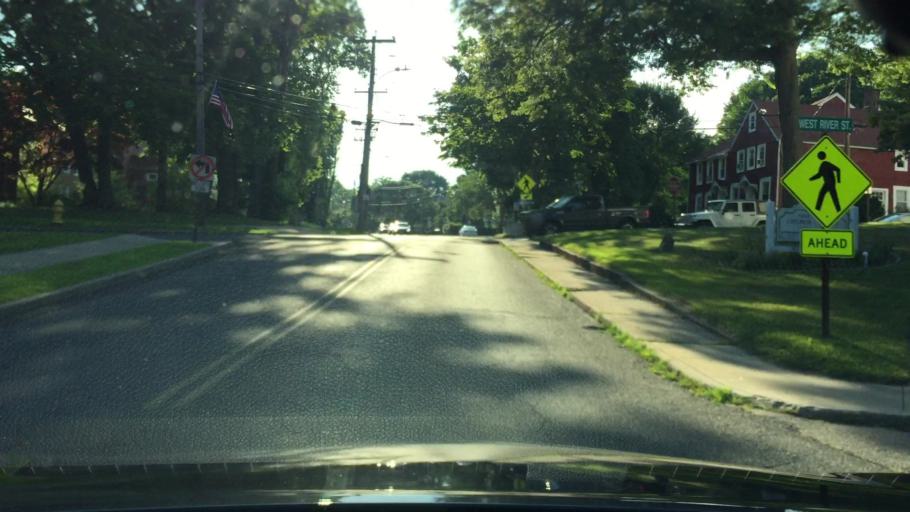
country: US
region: Connecticut
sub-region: New Haven County
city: City of Milford (balance)
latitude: 41.2266
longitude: -73.0585
